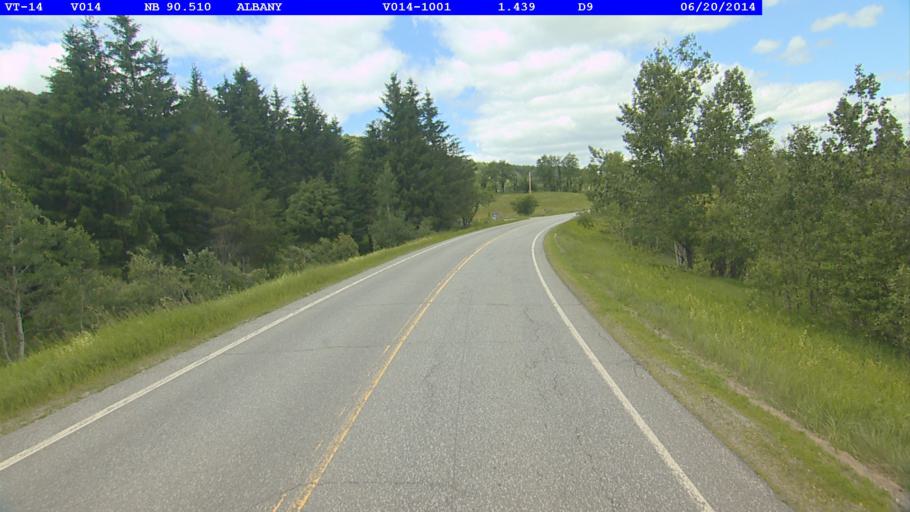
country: US
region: Vermont
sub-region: Caledonia County
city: Hardwick
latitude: 44.7223
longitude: -72.3839
